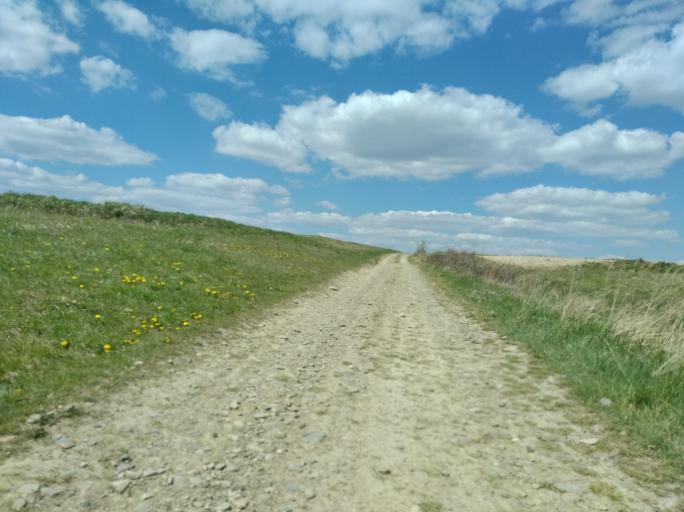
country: PL
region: Subcarpathian Voivodeship
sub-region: Powiat brzozowski
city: Jablonka
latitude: 49.7417
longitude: 22.0862
